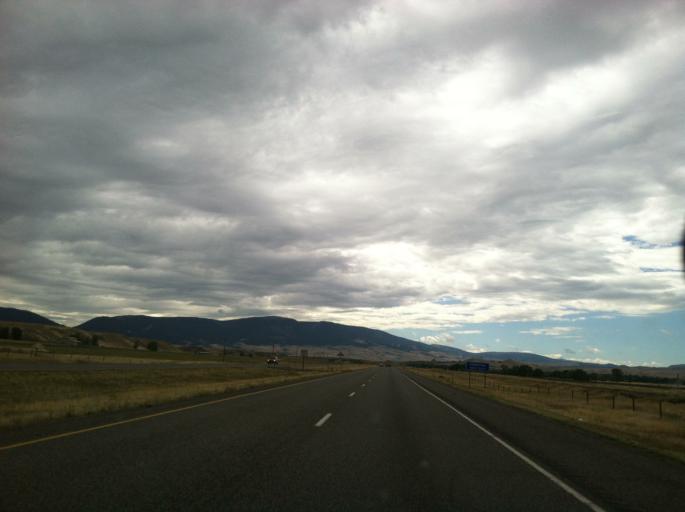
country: US
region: Montana
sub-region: Park County
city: Livingston
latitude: 45.6927
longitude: -110.4907
